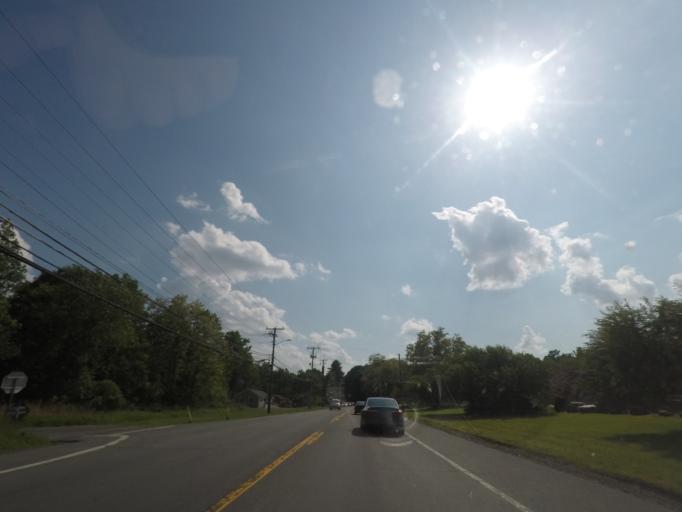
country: US
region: New York
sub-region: Orange County
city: Balmville
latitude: 41.5658
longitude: -73.9983
